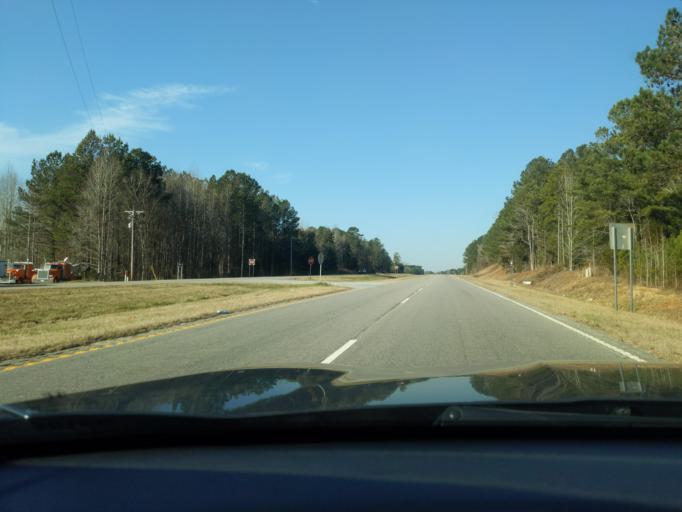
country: US
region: South Carolina
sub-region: Greenwood County
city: Greenwood
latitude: 34.1897
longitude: -82.2594
